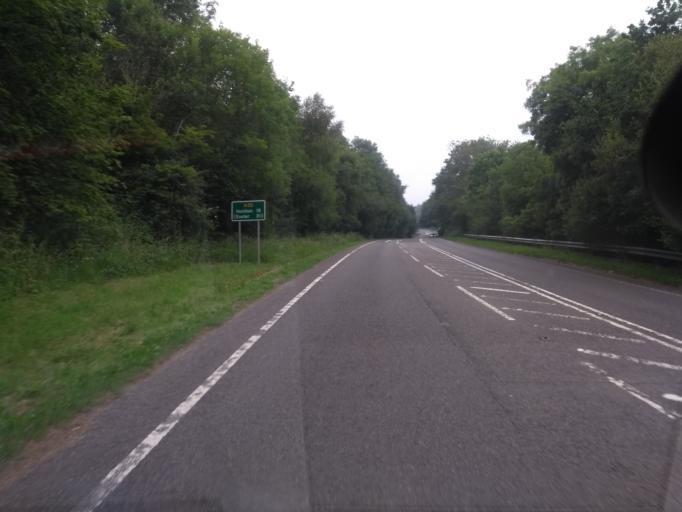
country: GB
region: England
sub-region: Dorset
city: Lyme Regis
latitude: 50.7439
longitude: -2.9205
